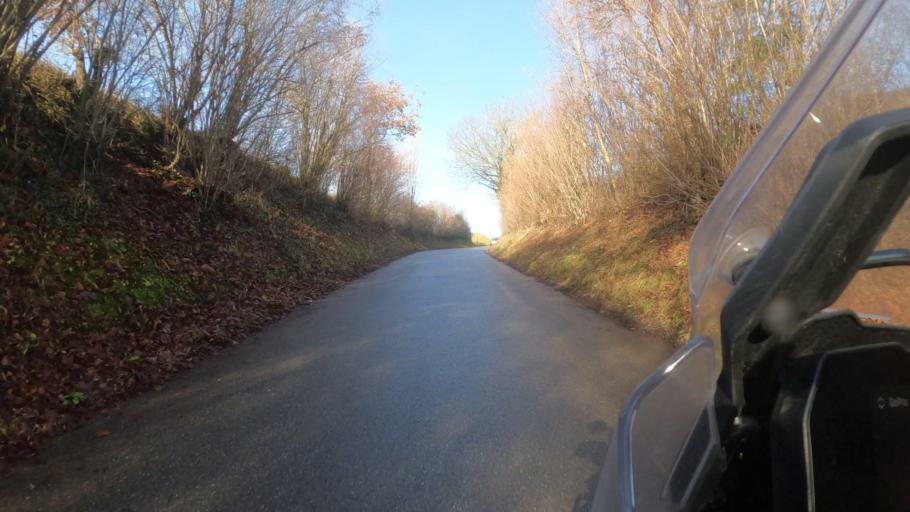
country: CH
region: Schaffhausen
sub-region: Bezirk Reiat
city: Thayngen
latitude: 47.7558
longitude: 8.7043
